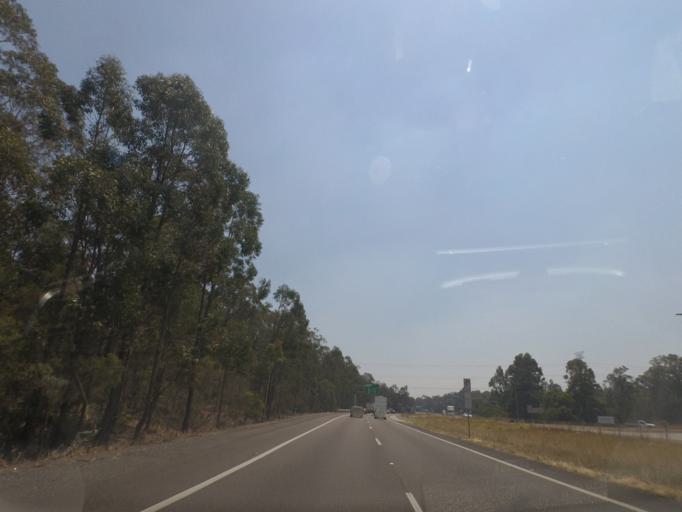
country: AU
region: New South Wales
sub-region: Newcastle
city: Beresfield
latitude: -32.8205
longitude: 151.6341
